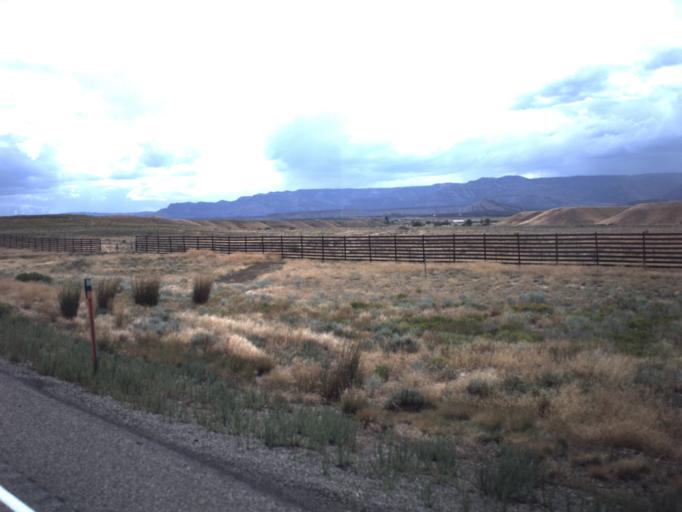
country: US
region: Utah
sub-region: Carbon County
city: Price
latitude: 39.5025
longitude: -110.8391
